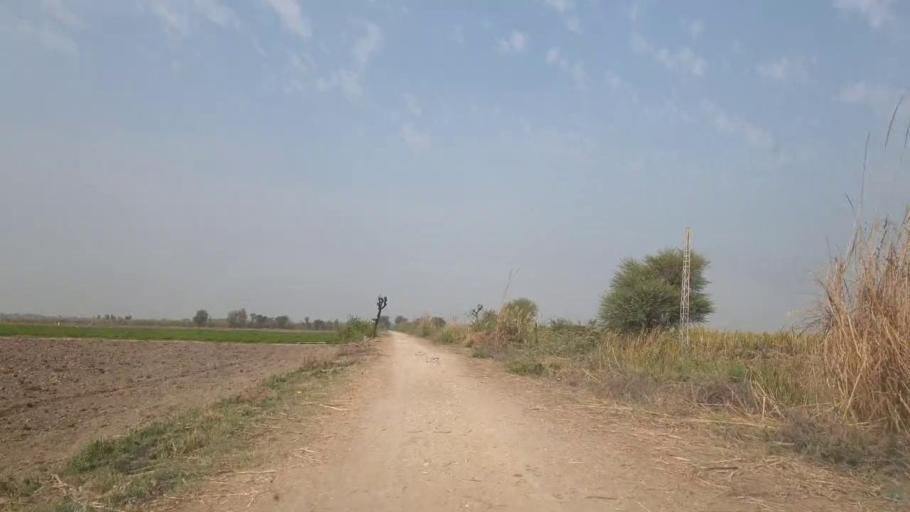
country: PK
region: Sindh
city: Mirpur Khas
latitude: 25.5622
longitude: 69.1063
